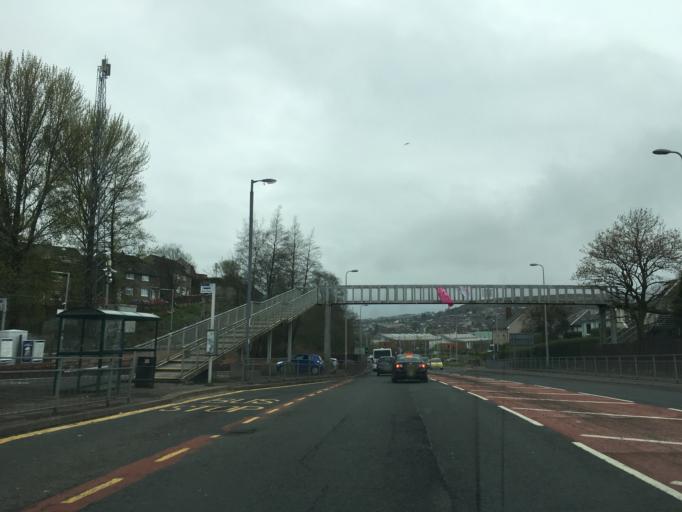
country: GB
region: Scotland
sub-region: Inverclyde
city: Gourock
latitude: 55.9409
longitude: -4.8030
